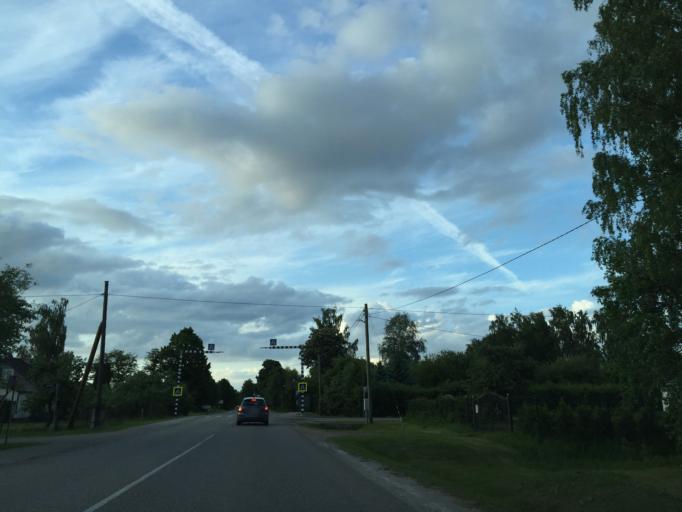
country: LV
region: Babite
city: Pinki
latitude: 56.9517
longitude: 23.9132
